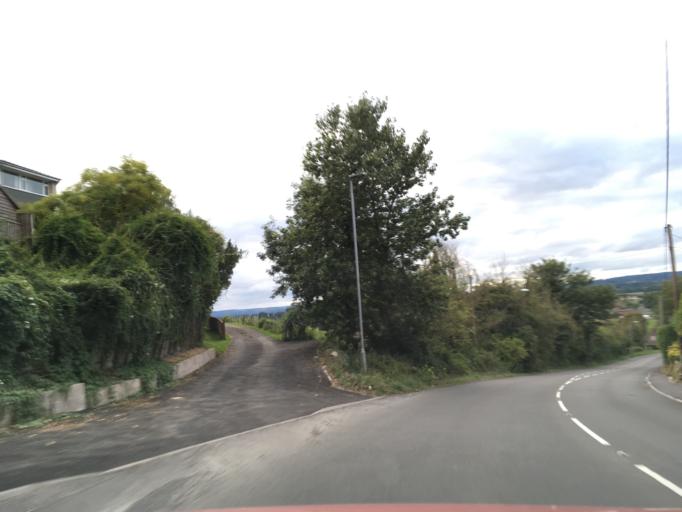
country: GB
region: England
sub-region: Wiltshire
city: Devizes
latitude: 51.3544
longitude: -2.0079
